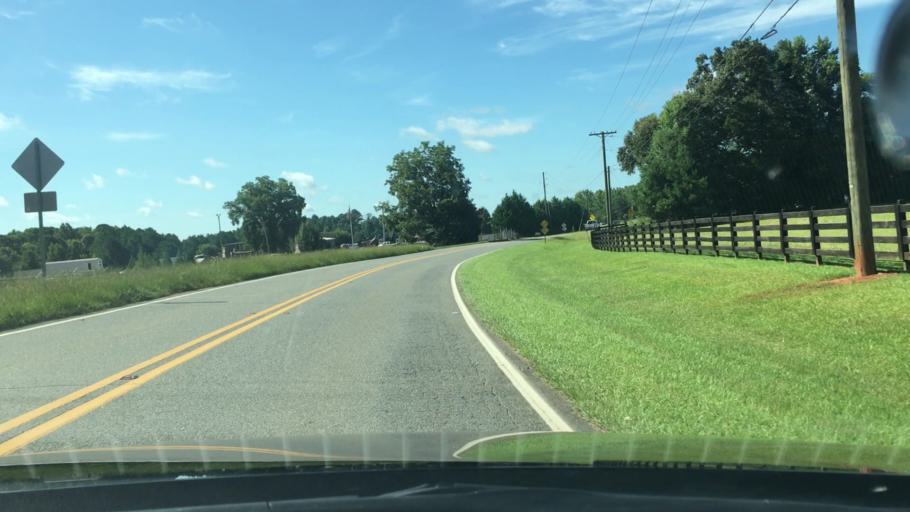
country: US
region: Georgia
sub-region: Putnam County
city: Jefferson
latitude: 33.4412
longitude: -83.2815
